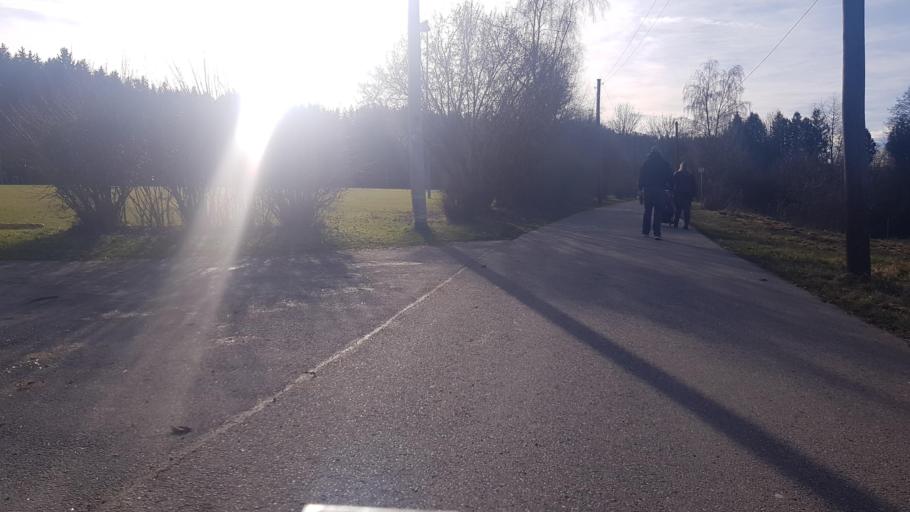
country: DE
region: Bavaria
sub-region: Upper Bavaria
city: Gauting
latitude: 48.0579
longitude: 11.3798
